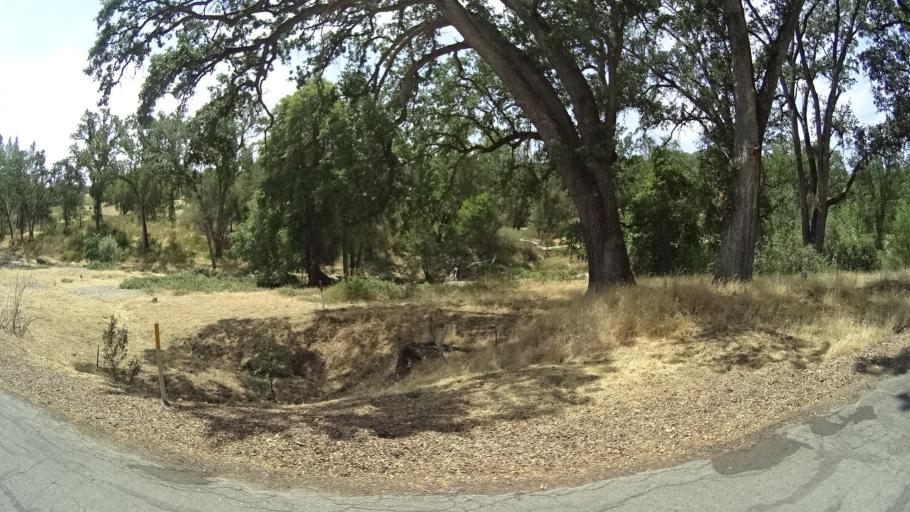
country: US
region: California
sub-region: Mariposa County
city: Mariposa
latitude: 37.4172
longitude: -119.8680
